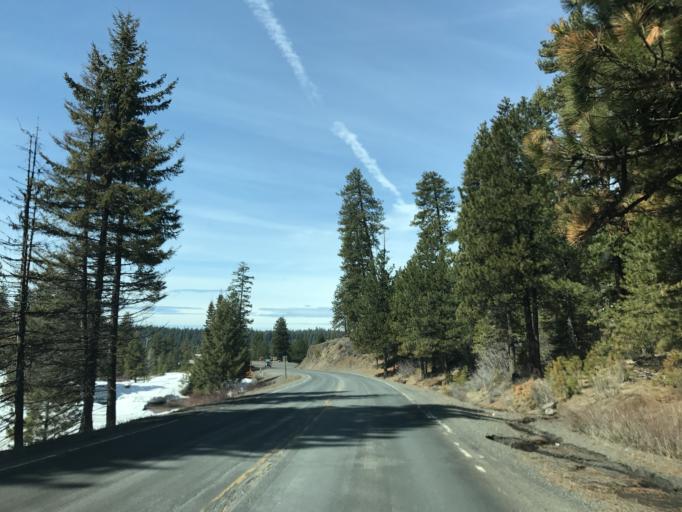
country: US
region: Idaho
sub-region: Valley County
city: McCall
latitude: 44.9301
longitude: -116.1590
